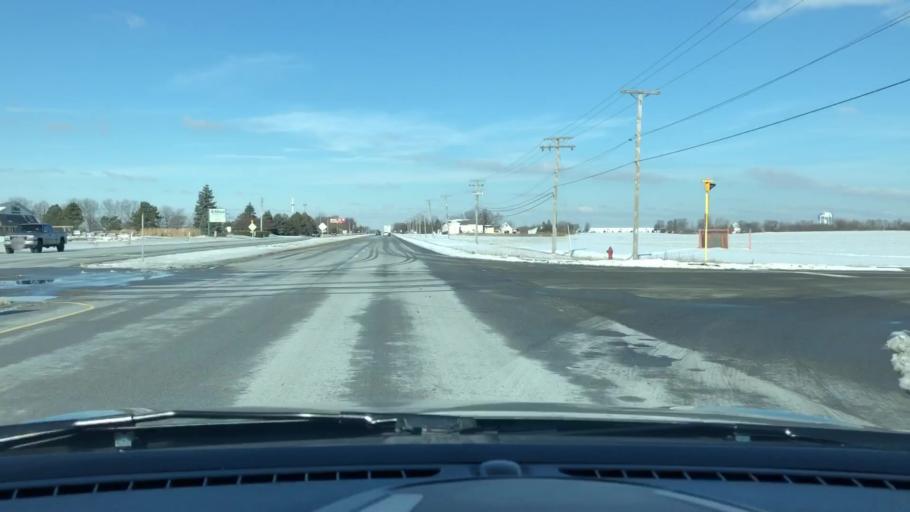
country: US
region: Illinois
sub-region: Will County
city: Preston Heights
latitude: 41.4663
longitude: -88.0795
